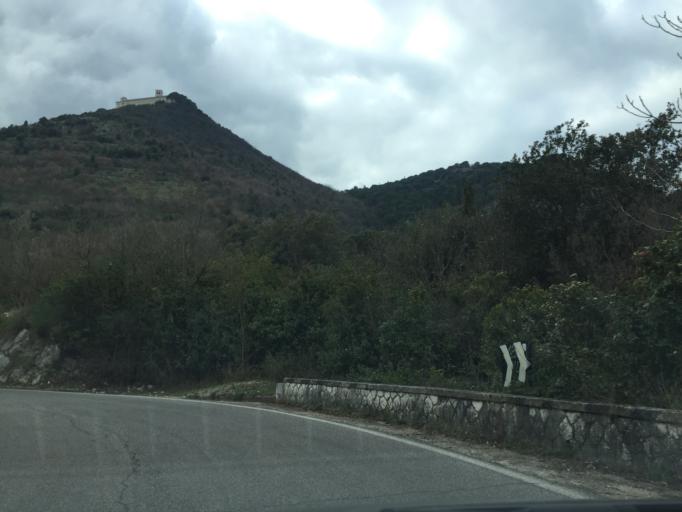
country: IT
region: Latium
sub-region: Provincia di Frosinone
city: Cassino
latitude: 41.4947
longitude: 13.8225
